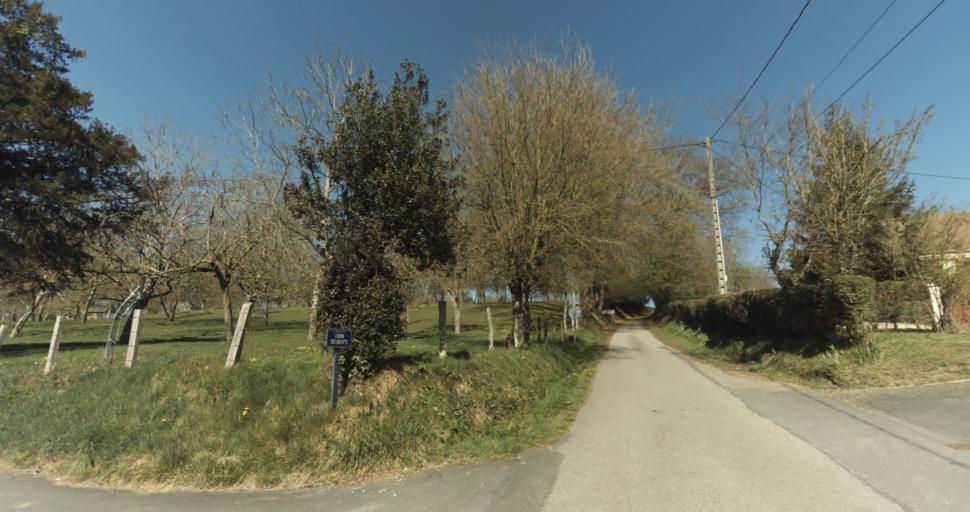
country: FR
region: Lower Normandy
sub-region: Departement du Calvados
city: Livarot
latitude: 49.0153
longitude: 0.0873
